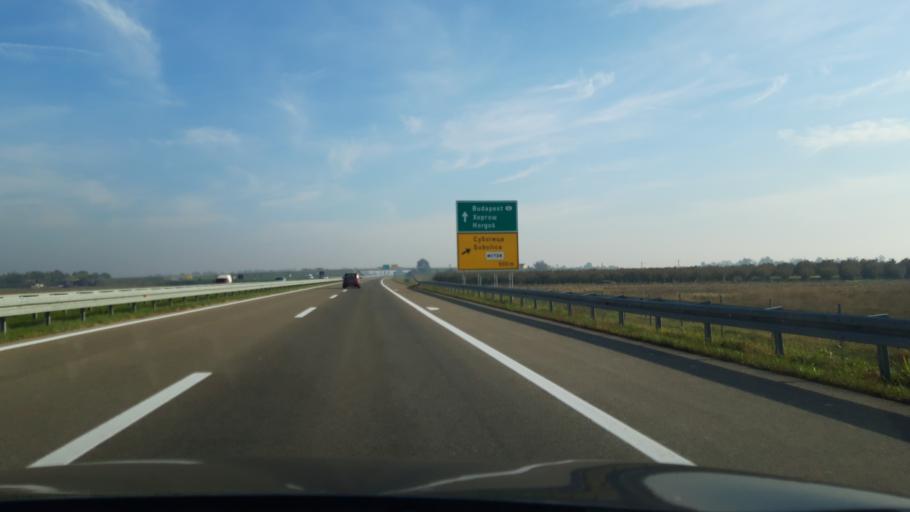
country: RS
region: Autonomna Pokrajina Vojvodina
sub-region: Severnobacki Okrug
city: Subotica
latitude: 46.0521
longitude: 19.7552
